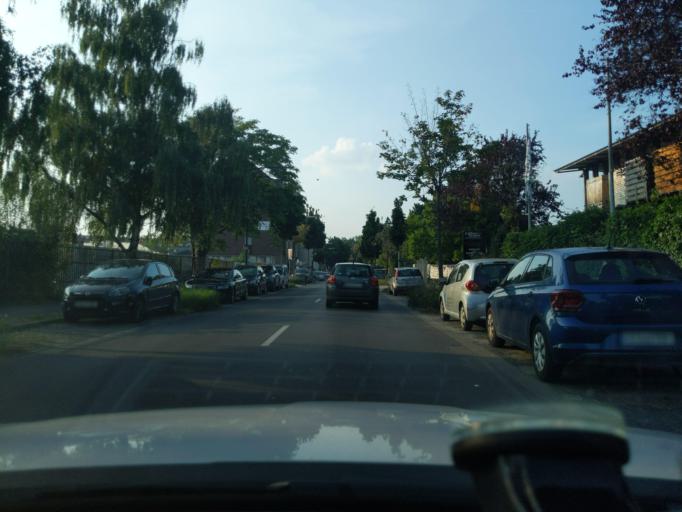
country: DE
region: North Rhine-Westphalia
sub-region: Regierungsbezirk Dusseldorf
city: Dusseldorf
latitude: 51.2099
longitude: 6.8125
